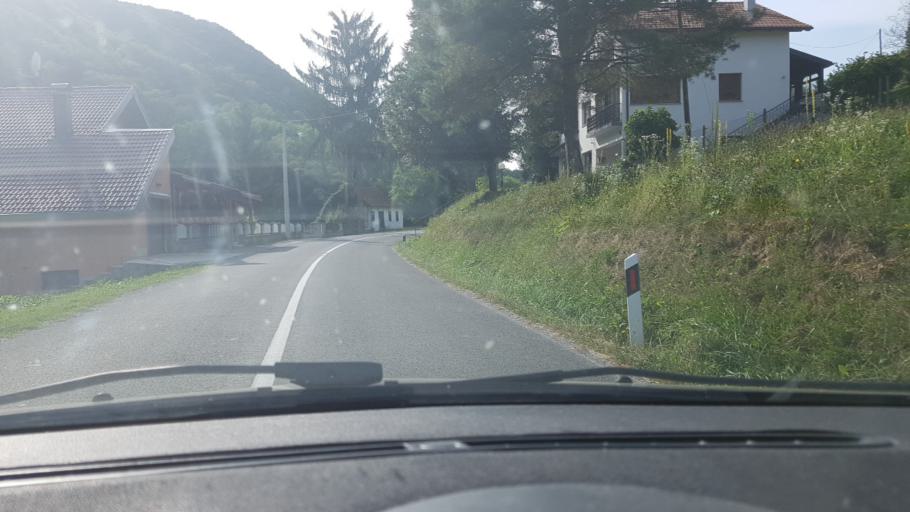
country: HR
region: Krapinsko-Zagorska
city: Mihovljan
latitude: 46.1196
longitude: 15.9993
